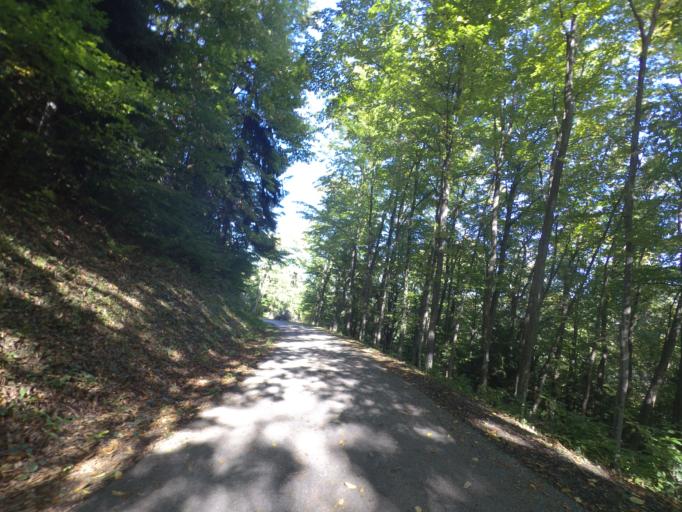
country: AT
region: Styria
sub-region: Politischer Bezirk Leibnitz
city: Kitzeck im Sausal
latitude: 46.7822
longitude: 15.4339
